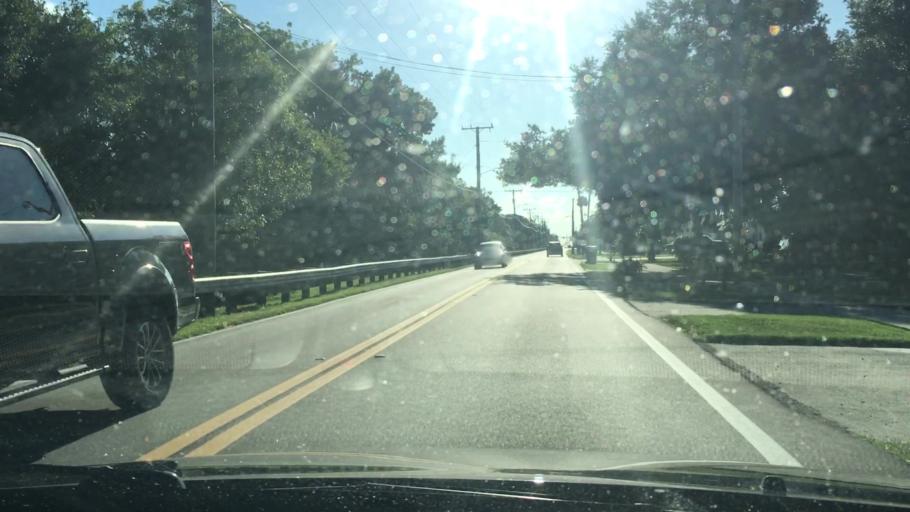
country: US
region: Florida
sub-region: Volusia County
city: Holly Hill
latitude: 29.2411
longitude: -81.0529
